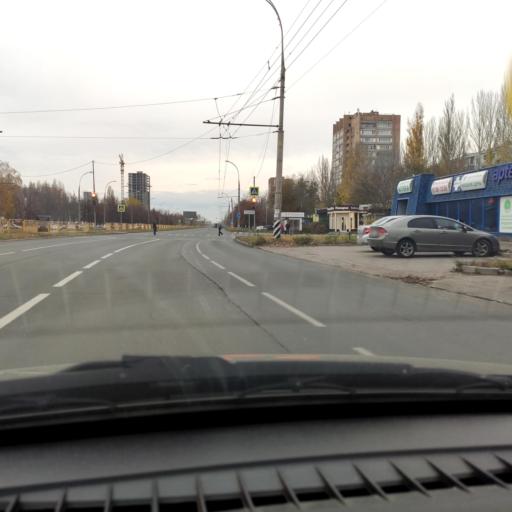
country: RU
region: Samara
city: Tol'yatti
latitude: 53.5212
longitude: 49.2956
